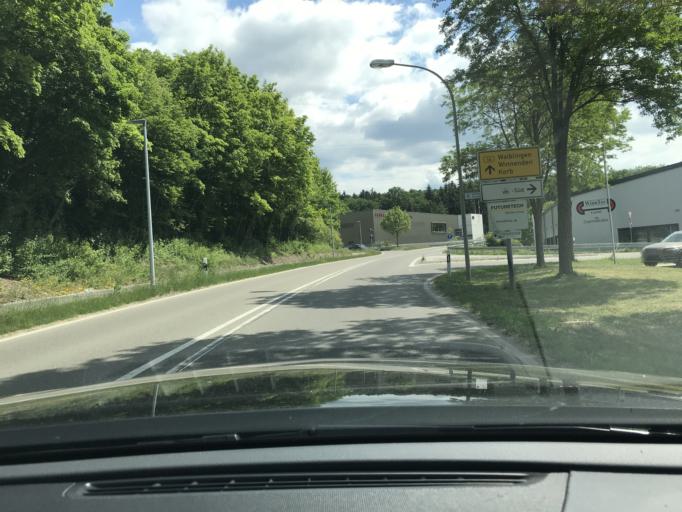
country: DE
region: Baden-Wuerttemberg
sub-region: Regierungsbezirk Stuttgart
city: Schwaikheim
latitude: 48.8694
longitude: 9.3616
